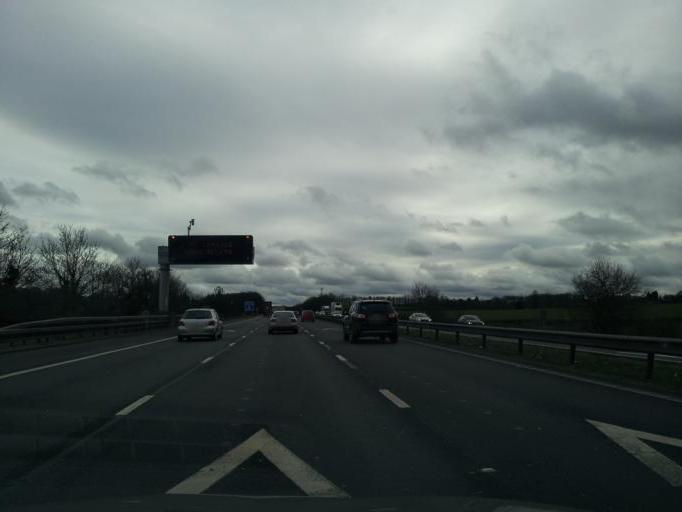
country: GB
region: England
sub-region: Staffordshire
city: Barlaston
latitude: 52.9304
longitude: -2.2112
